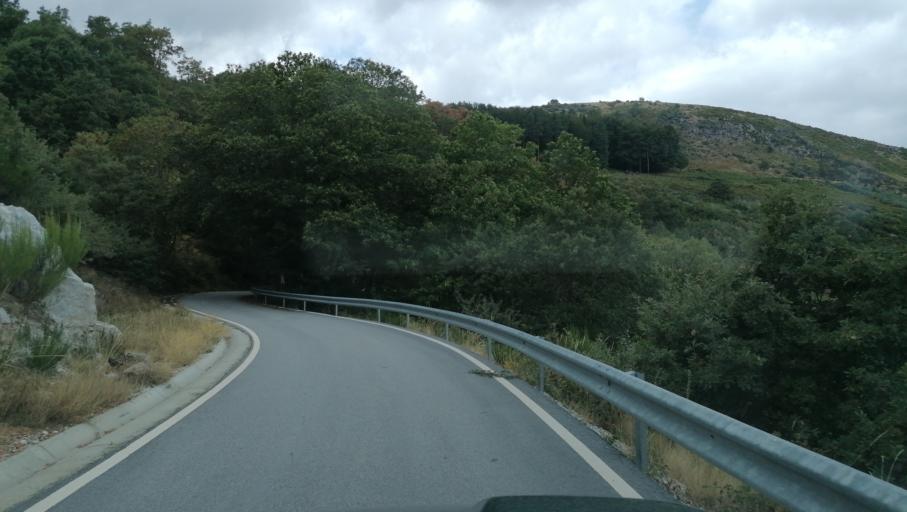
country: PT
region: Vila Real
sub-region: Vila Pouca de Aguiar
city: Vila Pouca de Aguiar
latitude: 41.5517
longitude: -7.6567
